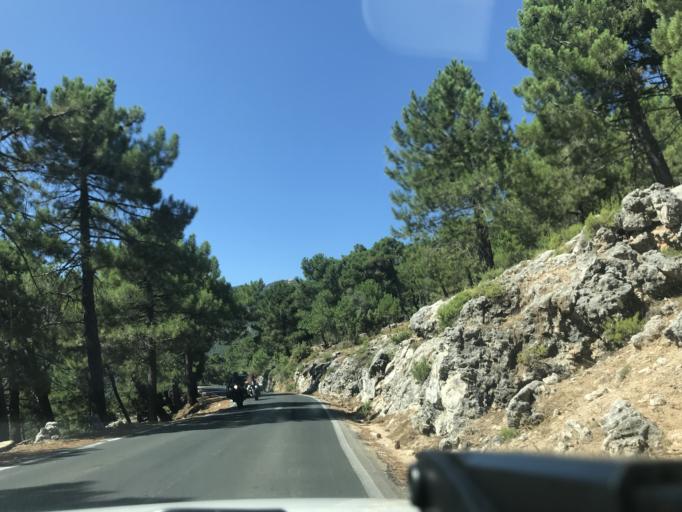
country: ES
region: Andalusia
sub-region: Provincia de Jaen
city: La Iruela
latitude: 37.9326
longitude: -2.9458
